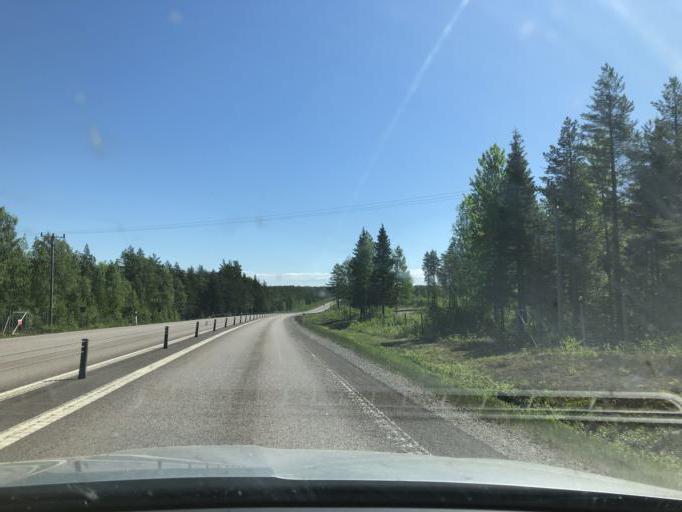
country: SE
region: Norrbotten
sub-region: Kalix Kommun
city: Toere
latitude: 65.9170
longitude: 22.7727
